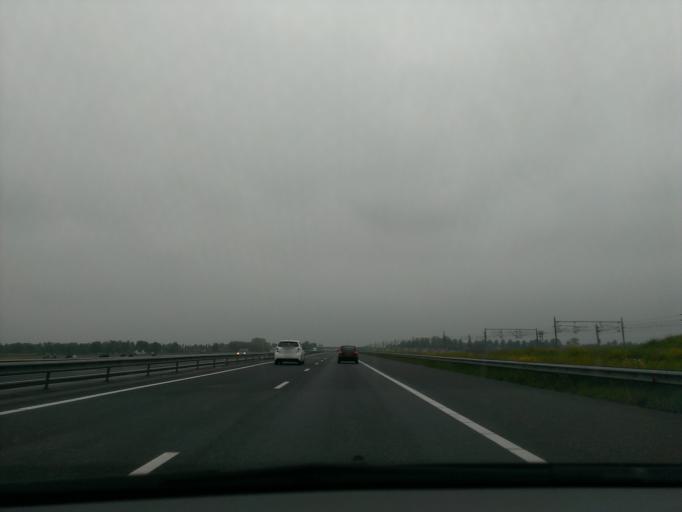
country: NL
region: Gelderland
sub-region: Gemeente Geldermalsen
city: Geldermalsen
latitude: 51.8591
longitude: 5.2952
